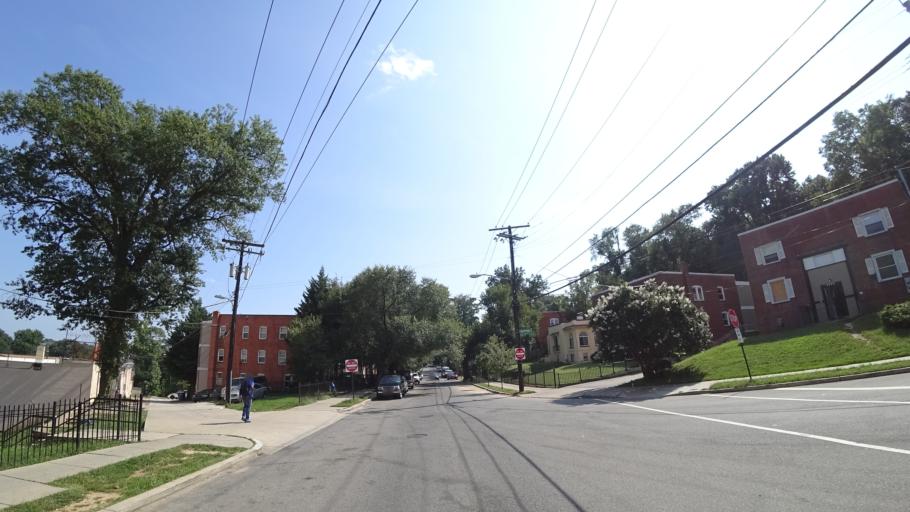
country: US
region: Maryland
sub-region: Prince George's County
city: Hillcrest Heights
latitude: 38.8536
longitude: -76.9657
